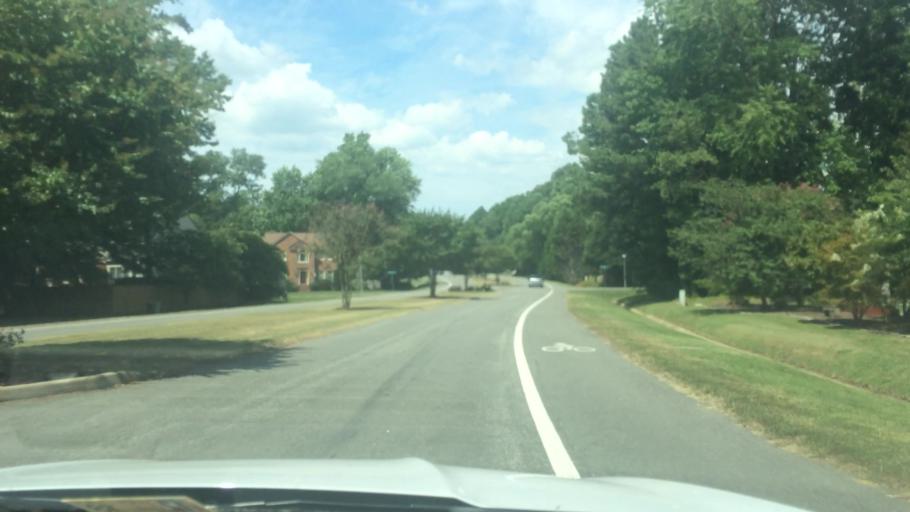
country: US
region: Virginia
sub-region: City of Poquoson
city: Poquoson
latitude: 37.1120
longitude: -76.4263
